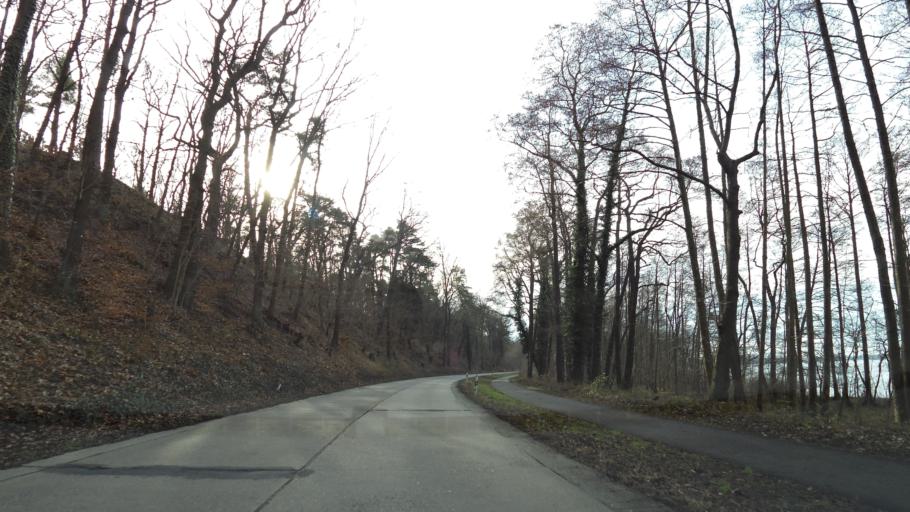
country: DE
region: Brandenburg
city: Michendorf
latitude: 52.3570
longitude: 13.0213
